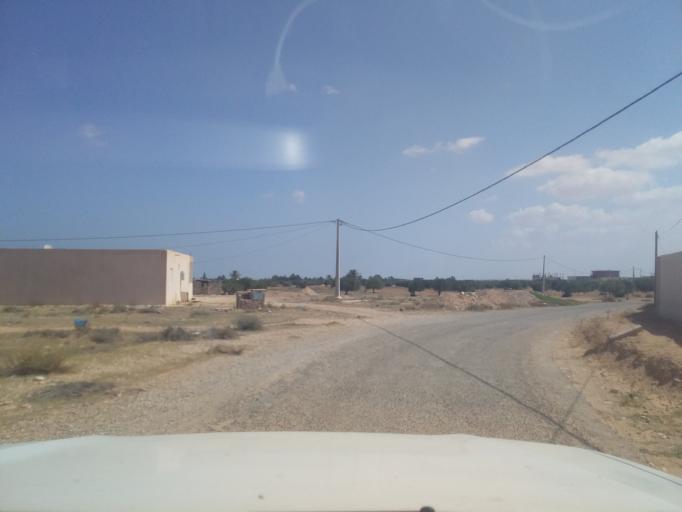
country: TN
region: Madanin
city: Medenine
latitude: 33.6115
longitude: 10.3070
